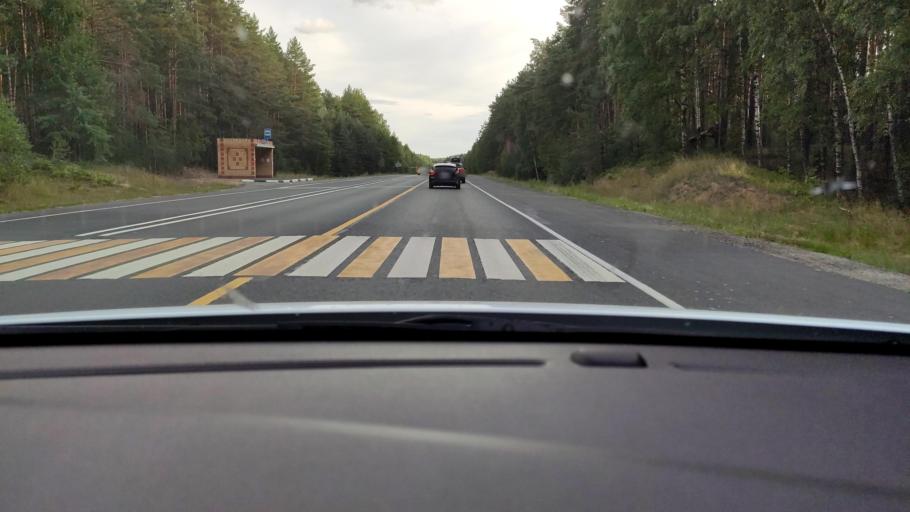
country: RU
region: Mariy-El
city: Pomary
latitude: 56.0206
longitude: 48.3809
